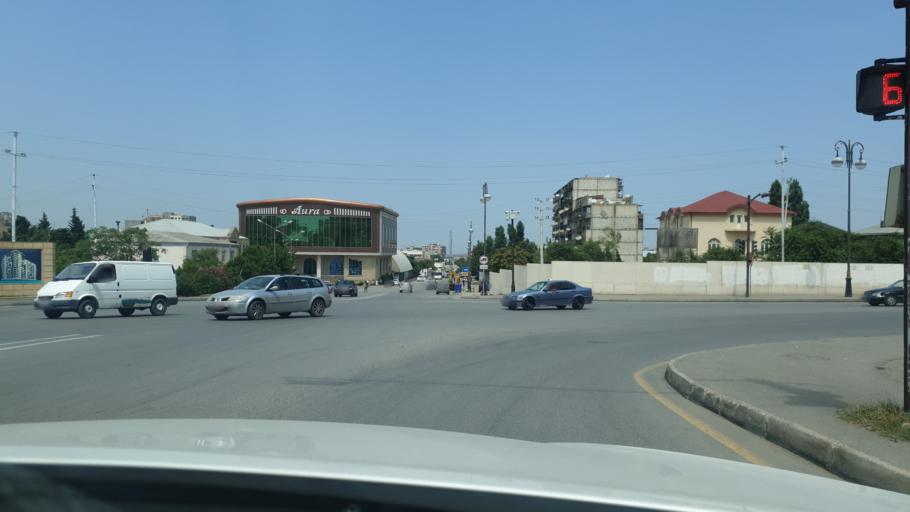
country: AZ
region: Baki
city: Qaracuxur
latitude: 40.3927
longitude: 49.9763
